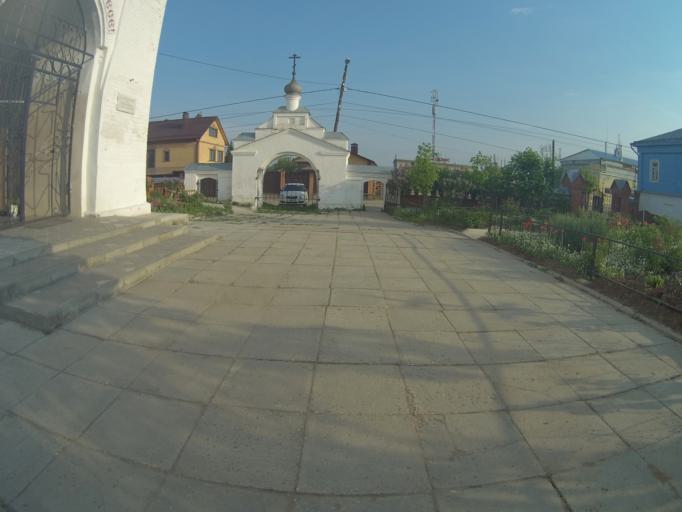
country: RU
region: Vladimir
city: Kommunar
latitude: 56.1626
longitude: 40.4451
